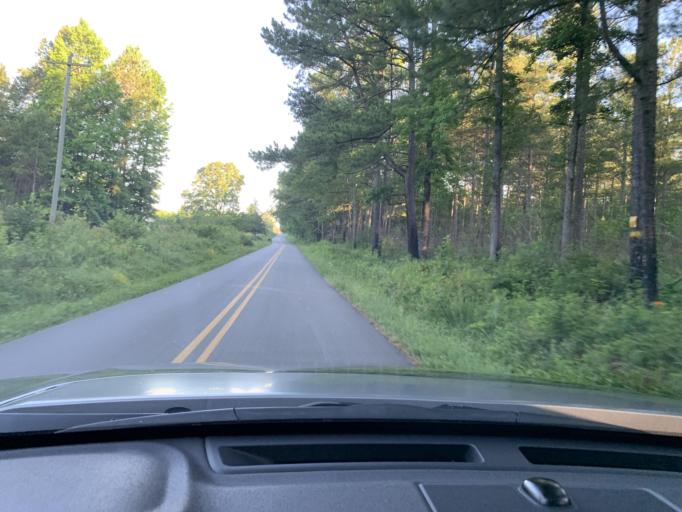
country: US
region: Georgia
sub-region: Bartow County
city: Rydal
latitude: 34.2572
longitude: -84.6933
